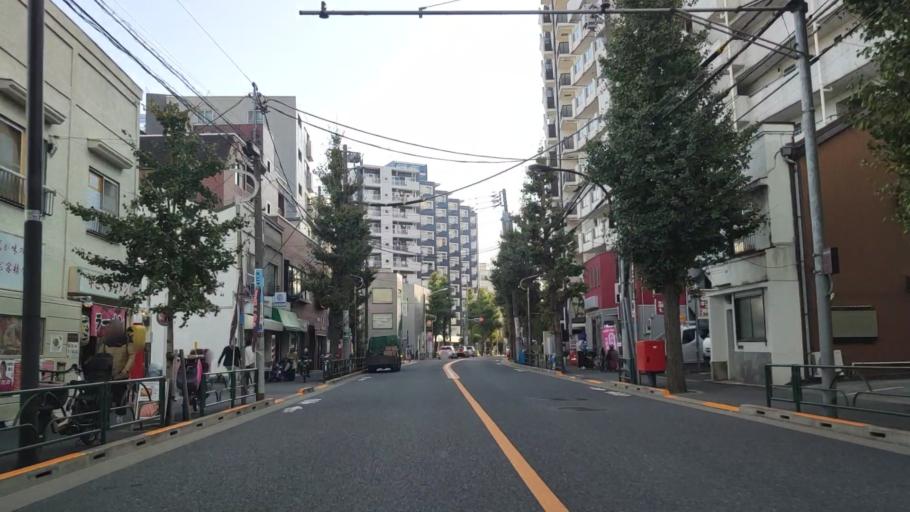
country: JP
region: Tokyo
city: Tokyo
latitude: 35.7002
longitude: 139.6673
